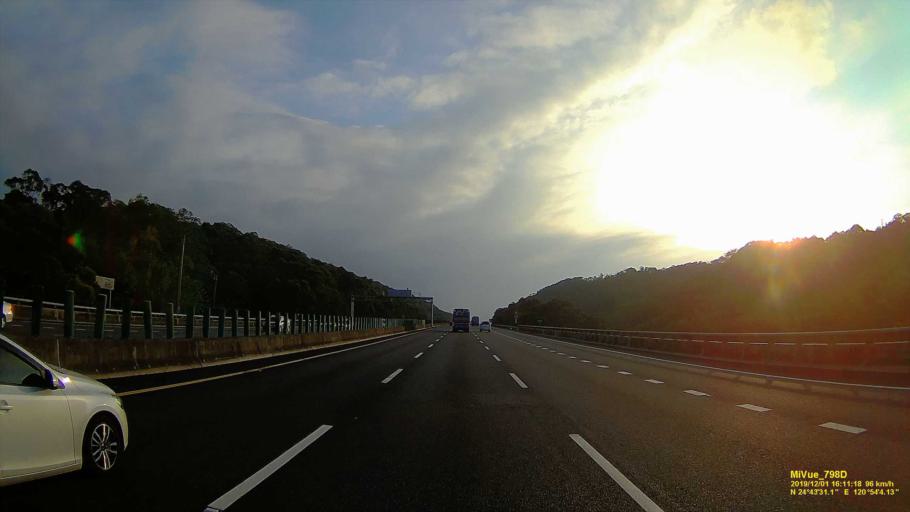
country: TW
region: Taiwan
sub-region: Hsinchu
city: Hsinchu
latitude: 24.7249
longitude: 120.9014
